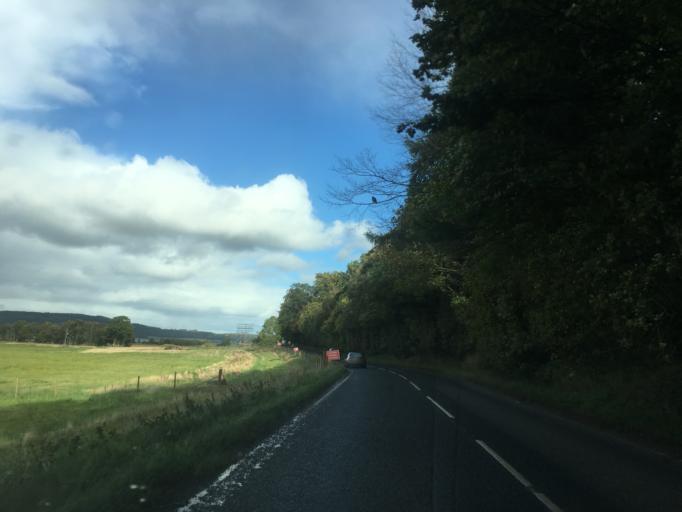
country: GB
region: Scotland
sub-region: Highland
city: Beauly
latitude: 57.4747
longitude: -4.3757
